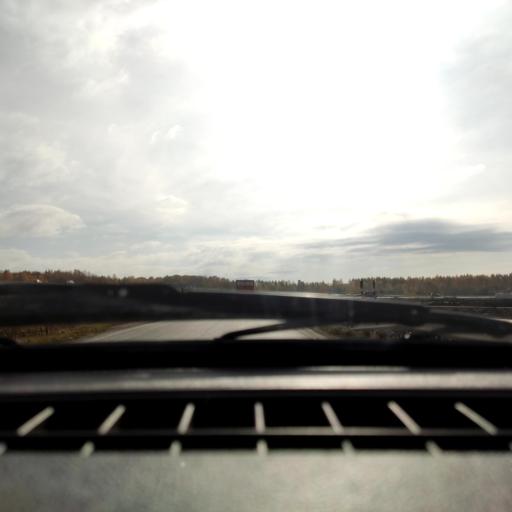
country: RU
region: Bashkortostan
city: Iglino
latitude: 54.7444
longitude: 56.3004
